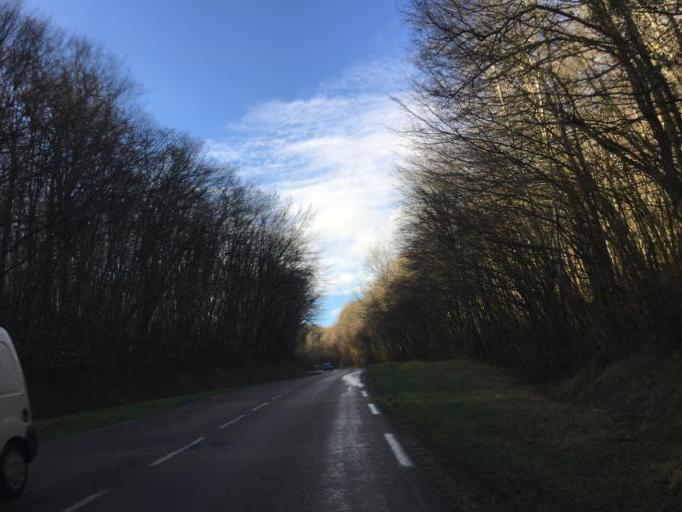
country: FR
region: Bourgogne
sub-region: Departement de la Nievre
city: Clamecy
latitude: 47.4554
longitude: 3.6420
